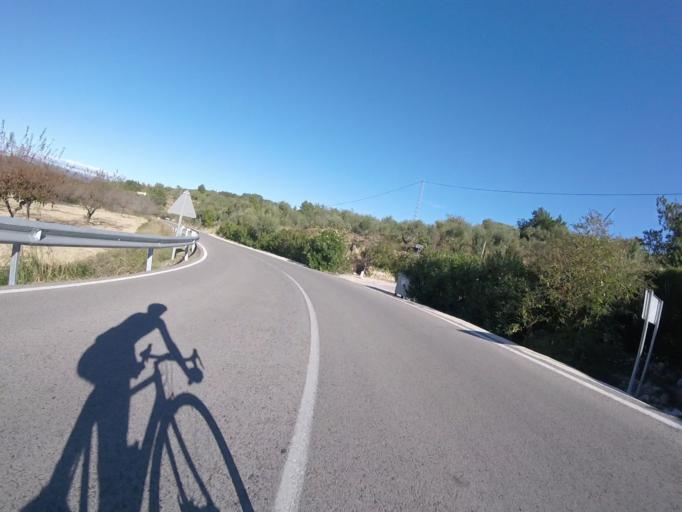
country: ES
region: Valencia
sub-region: Provincia de Castello
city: Cervera del Maestre
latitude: 40.4612
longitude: 0.2612
